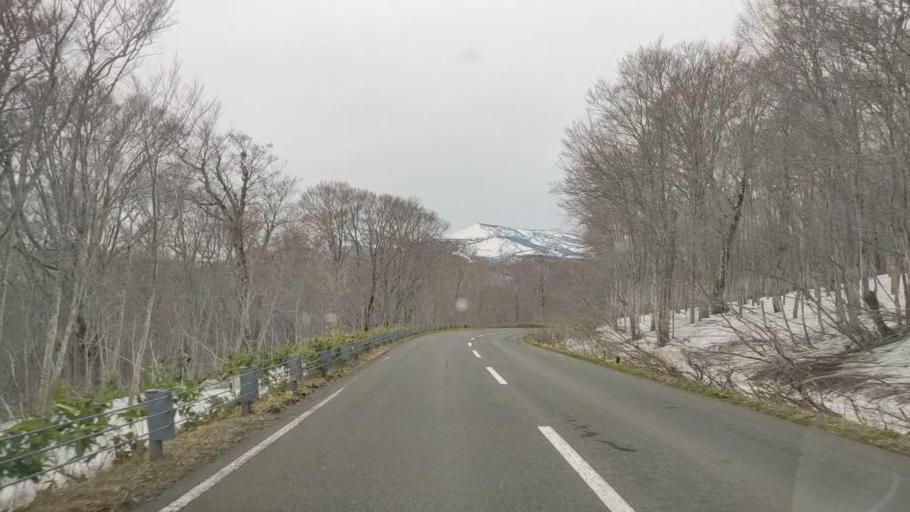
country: JP
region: Aomori
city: Aomori Shi
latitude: 40.6421
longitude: 140.9391
